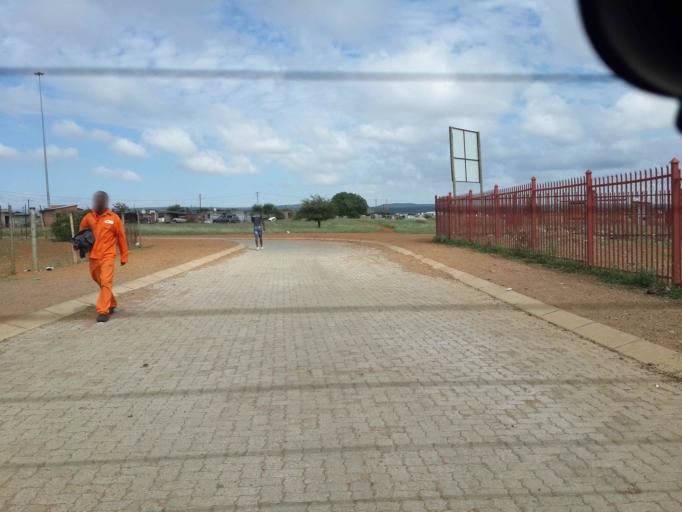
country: ZA
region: Northern Cape
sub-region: Siyanda District Municipality
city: Danielskuil
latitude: -28.1982
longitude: 23.5544
